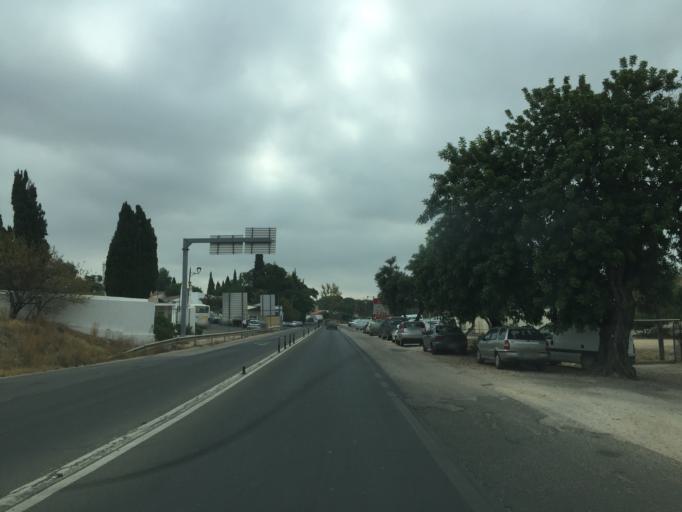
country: PT
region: Faro
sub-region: Loule
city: Almancil
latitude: 37.0824
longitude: -8.0117
